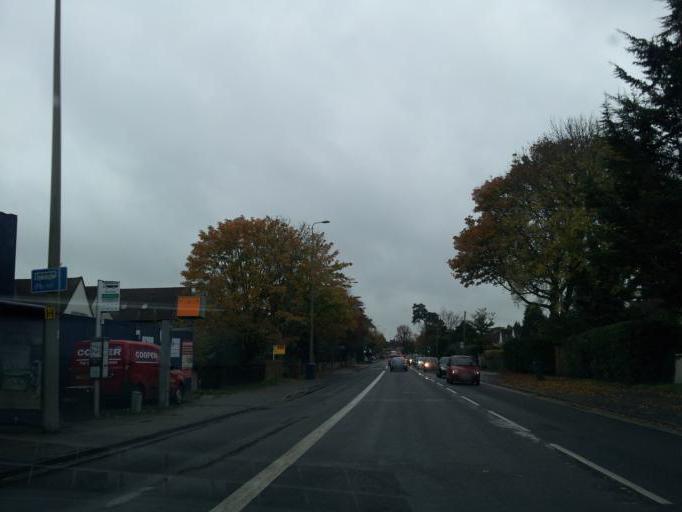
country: GB
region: England
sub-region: Oxfordshire
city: Kidlington
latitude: 51.7909
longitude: -1.2716
